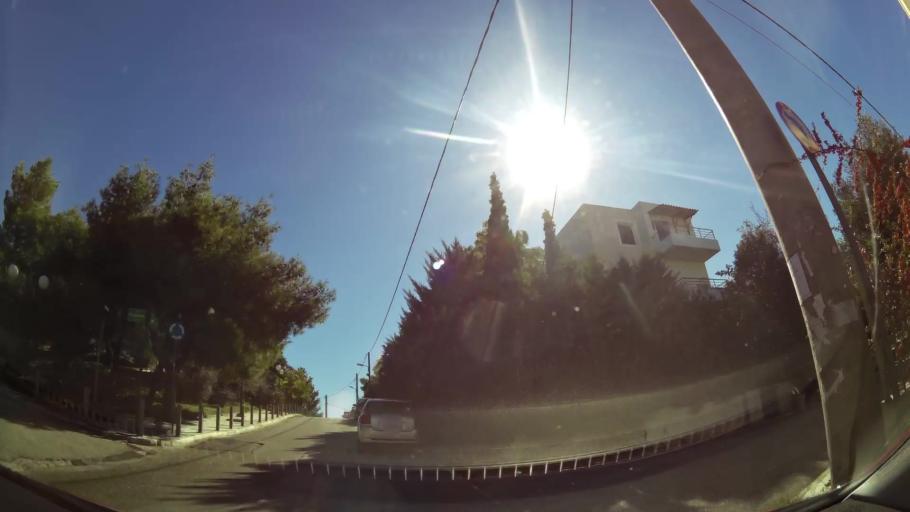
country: GR
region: Attica
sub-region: Nomarchia Anatolikis Attikis
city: Leondarion
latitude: 37.9858
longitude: 23.8569
